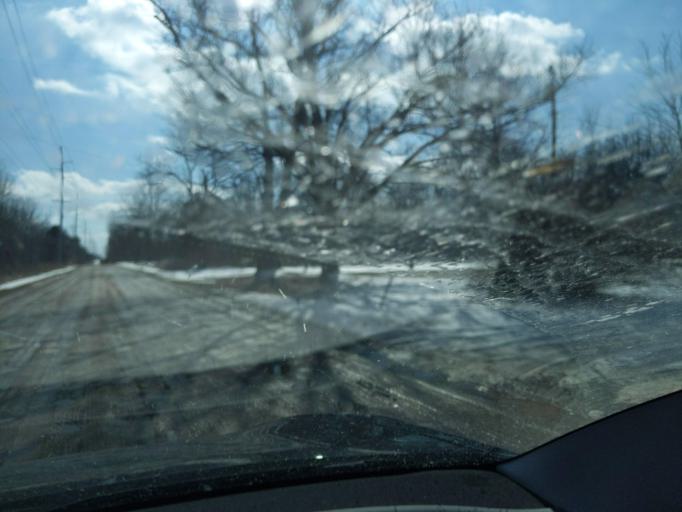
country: US
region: Michigan
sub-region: Livingston County
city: Fowlerville
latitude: 42.6282
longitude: -84.0914
